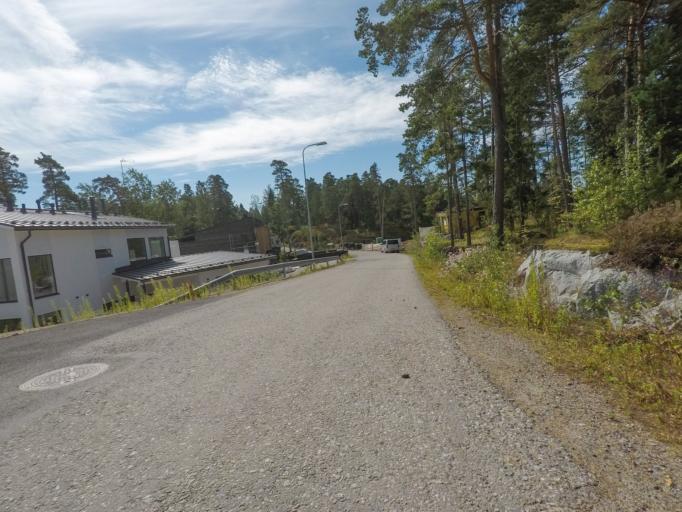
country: FI
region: Uusimaa
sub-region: Helsinki
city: Vantaa
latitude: 60.1678
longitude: 25.0913
